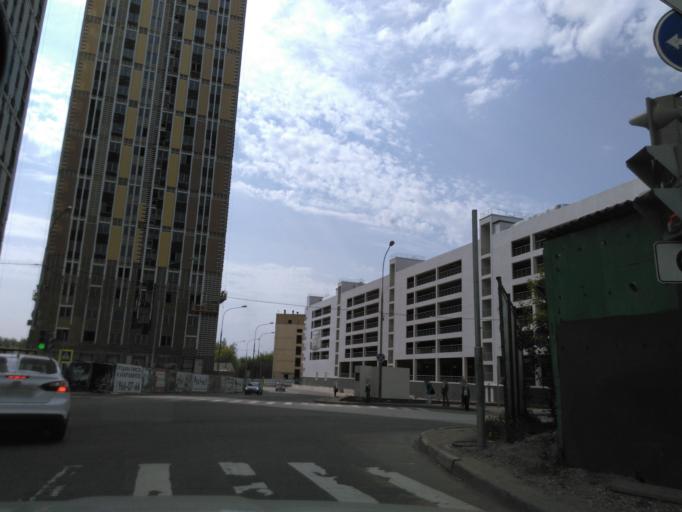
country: RU
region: Moscow
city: Golovinskiy
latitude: 55.8415
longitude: 37.4928
